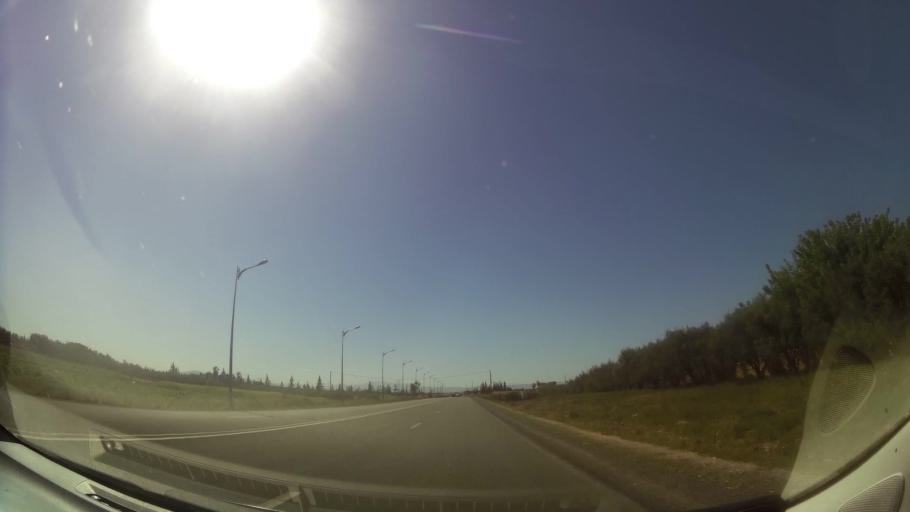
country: MA
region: Oriental
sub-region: Oujda-Angad
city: Oujda
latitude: 34.7372
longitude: -1.8820
